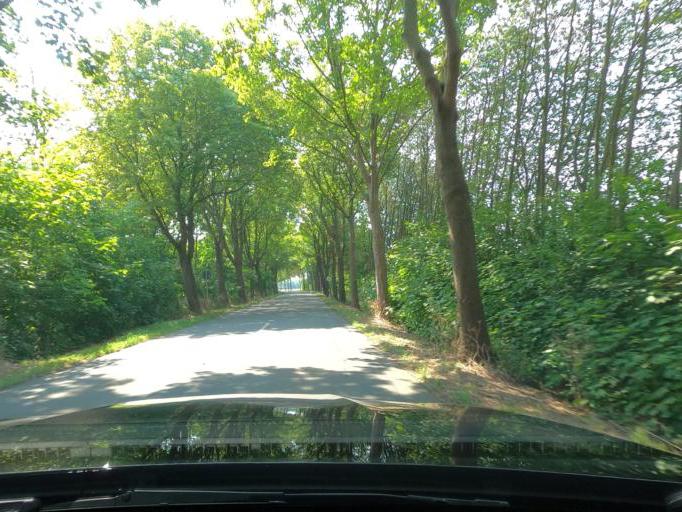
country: DE
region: Lower Saxony
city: Sarstedt
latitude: 52.2431
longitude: 9.8237
